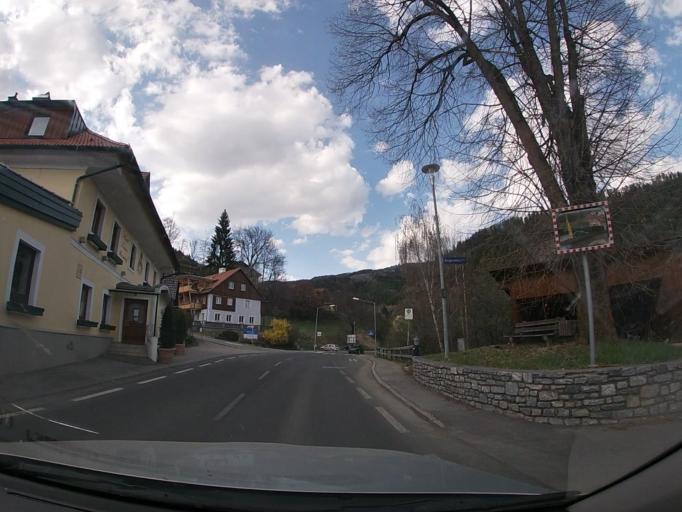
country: AT
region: Styria
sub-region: Politischer Bezirk Murau
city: Murau
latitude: 47.1152
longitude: 14.1703
